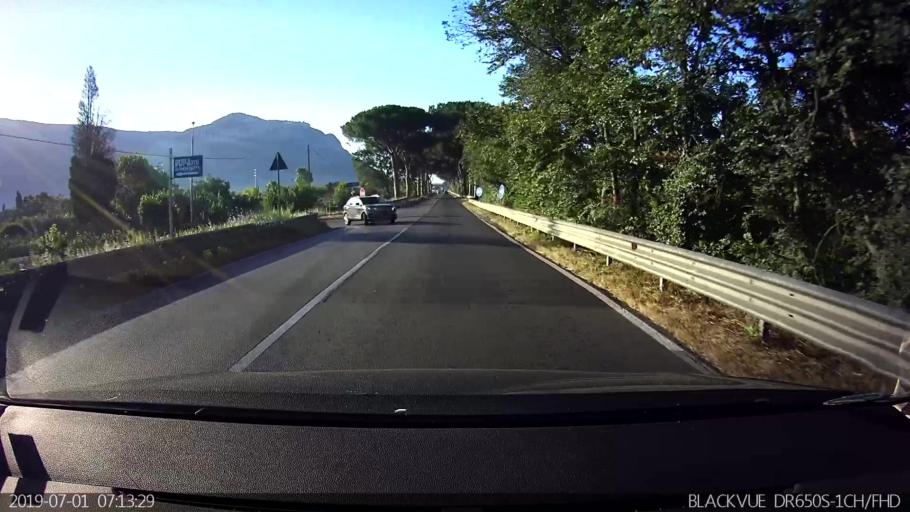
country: IT
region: Latium
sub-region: Provincia di Latina
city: Borgo Hermada
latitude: 41.3260
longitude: 13.1782
